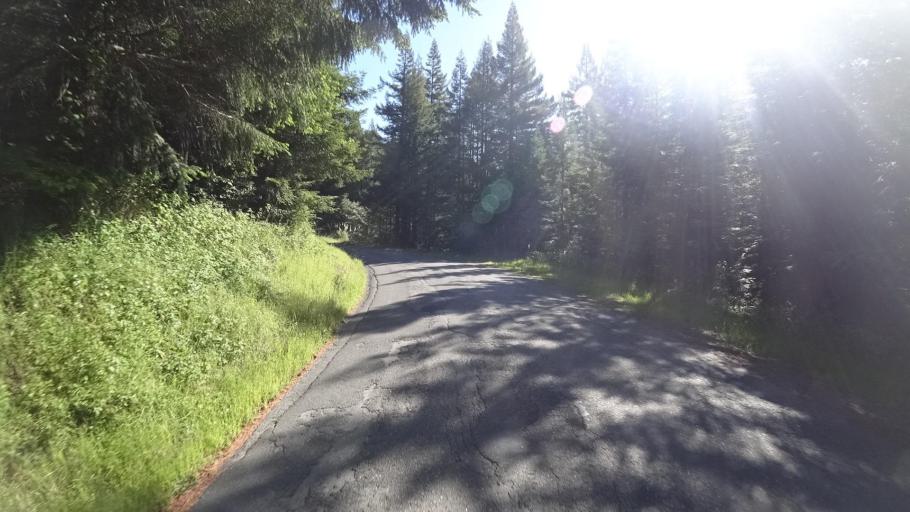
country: US
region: California
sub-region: Humboldt County
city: Rio Dell
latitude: 40.4576
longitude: -124.0166
